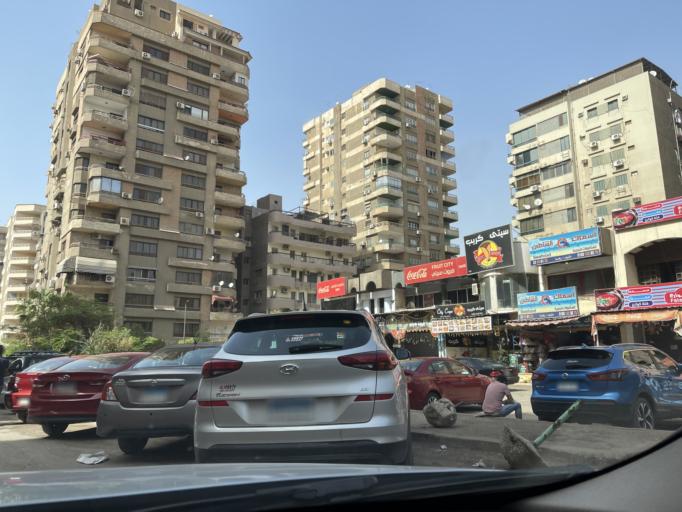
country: EG
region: Muhafazat al Qahirah
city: Cairo
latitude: 30.0639
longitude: 31.3505
